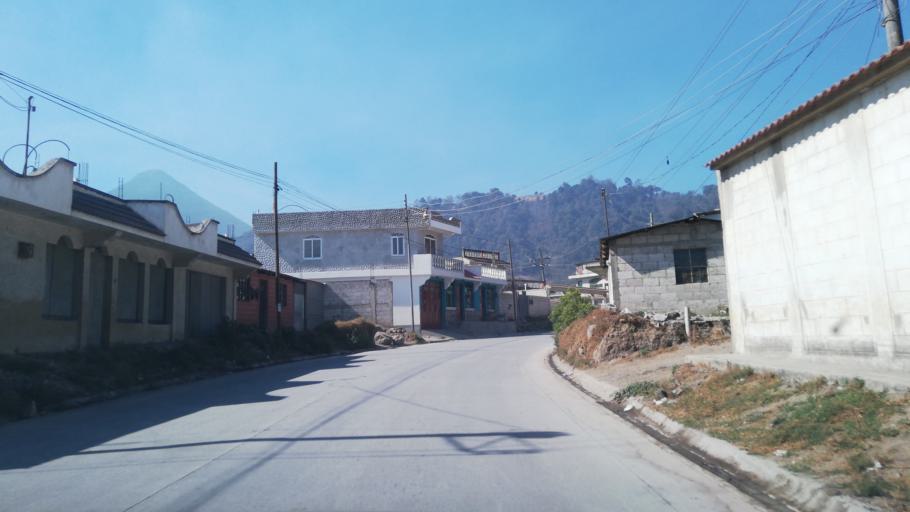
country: GT
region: Quetzaltenango
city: Quetzaltenango
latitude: 14.8071
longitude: -91.5529
